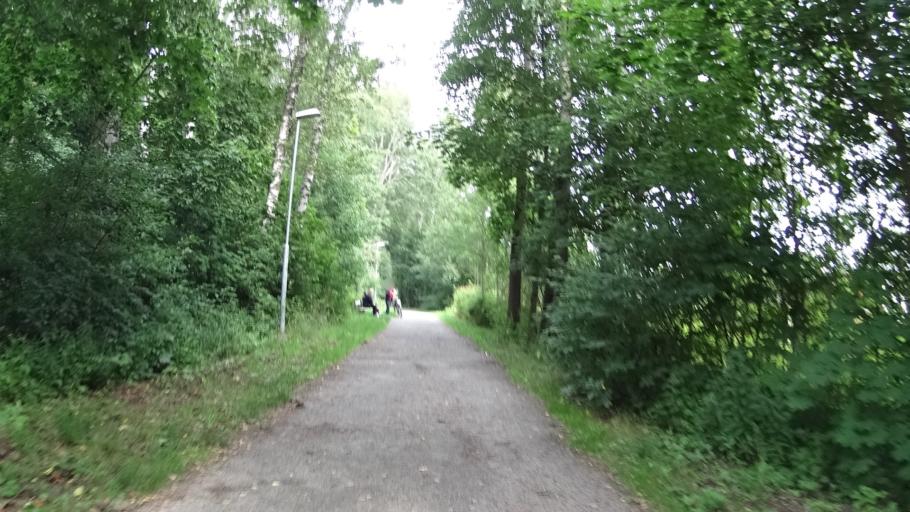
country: FI
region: Uusimaa
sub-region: Helsinki
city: Teekkarikylae
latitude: 60.2166
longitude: 24.8572
